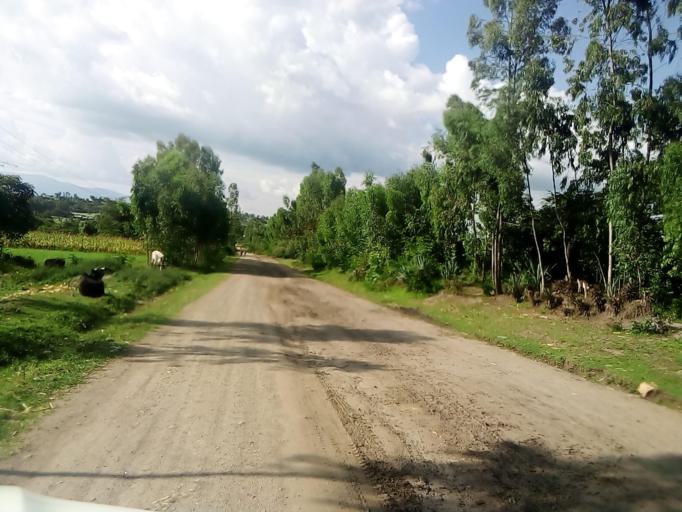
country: ET
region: Southern Nations, Nationalities, and People's Region
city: K'olito
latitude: 7.6589
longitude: 38.0479
